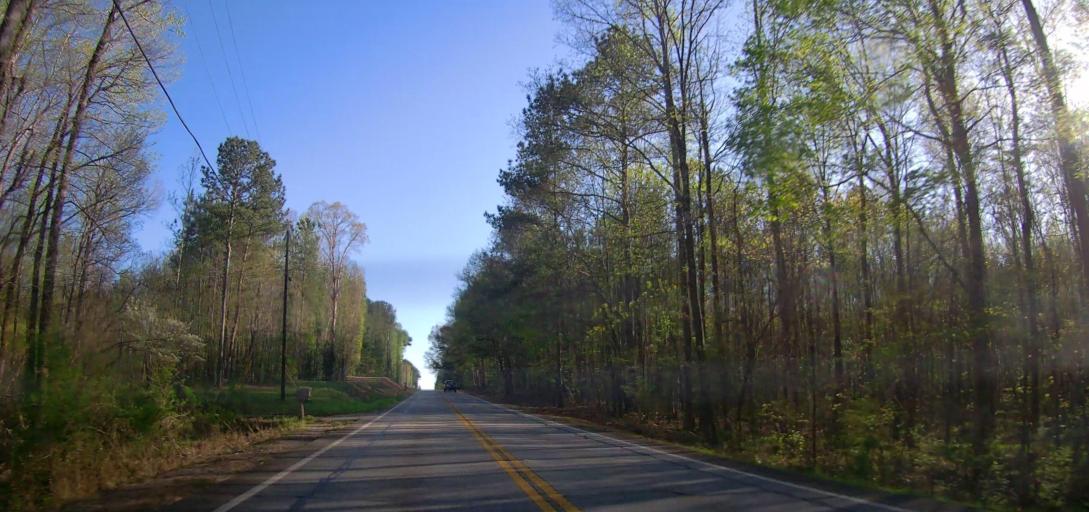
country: US
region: Georgia
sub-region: Butts County
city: Indian Springs
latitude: 33.2083
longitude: -83.9348
